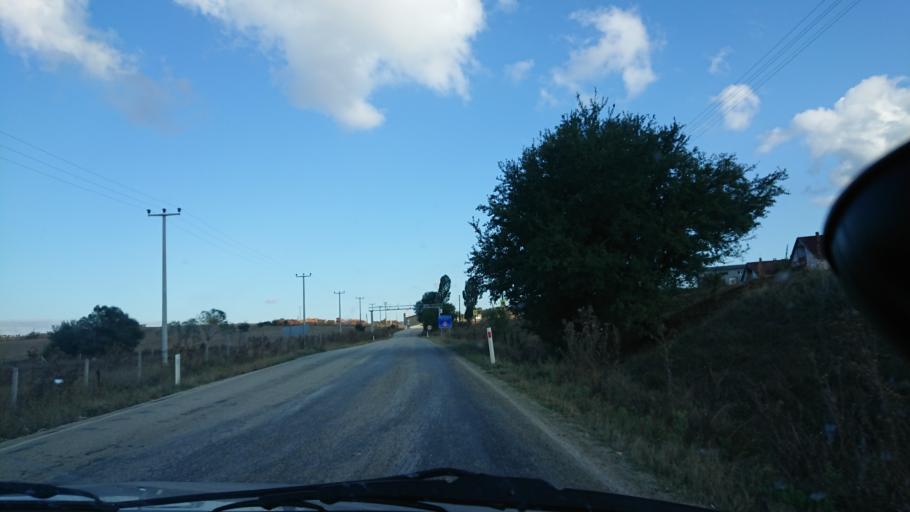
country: TR
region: Bilecik
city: Pazaryeri
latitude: 40.0019
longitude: 29.8837
